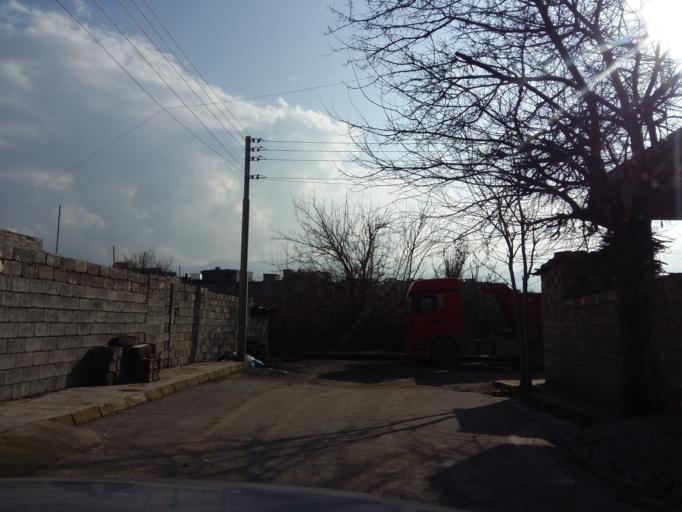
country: IQ
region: As Sulaymaniyah
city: Qeladize
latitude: 36.1759
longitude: 45.1397
